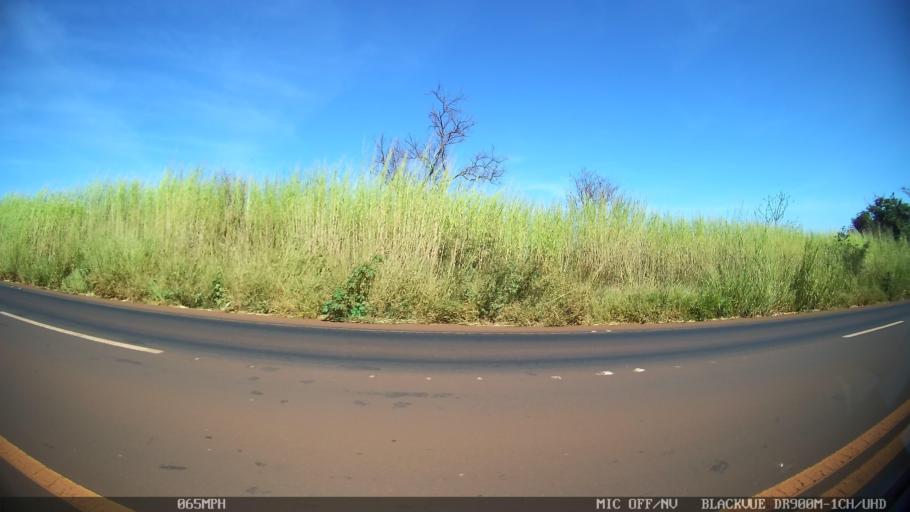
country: BR
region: Sao Paulo
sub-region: Sao Joaquim Da Barra
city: Sao Joaquim da Barra
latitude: -20.5490
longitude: -47.7556
